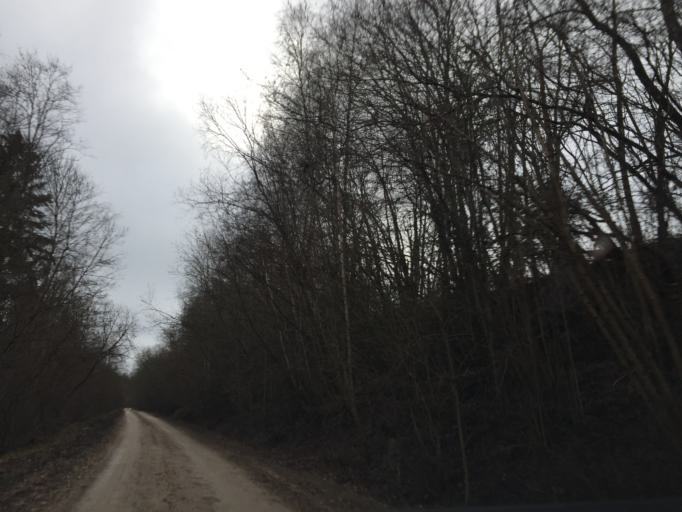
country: LV
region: Broceni
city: Broceni
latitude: 56.6827
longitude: 22.5578
